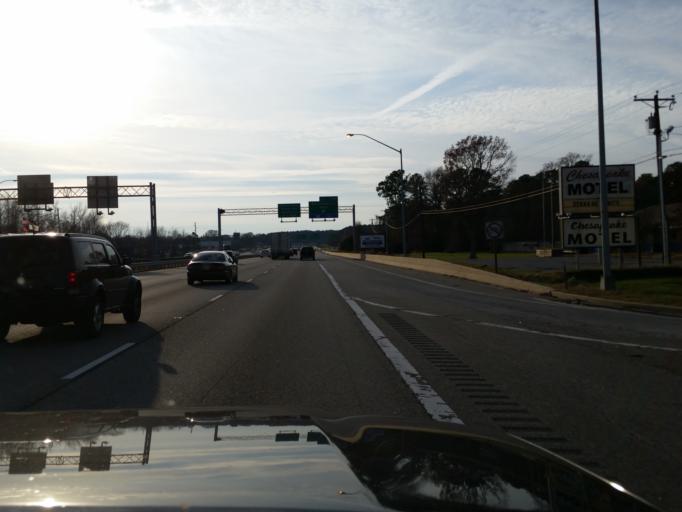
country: US
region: Maryland
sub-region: Queen Anne's County
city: Grasonville
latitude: 38.9655
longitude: -76.1926
